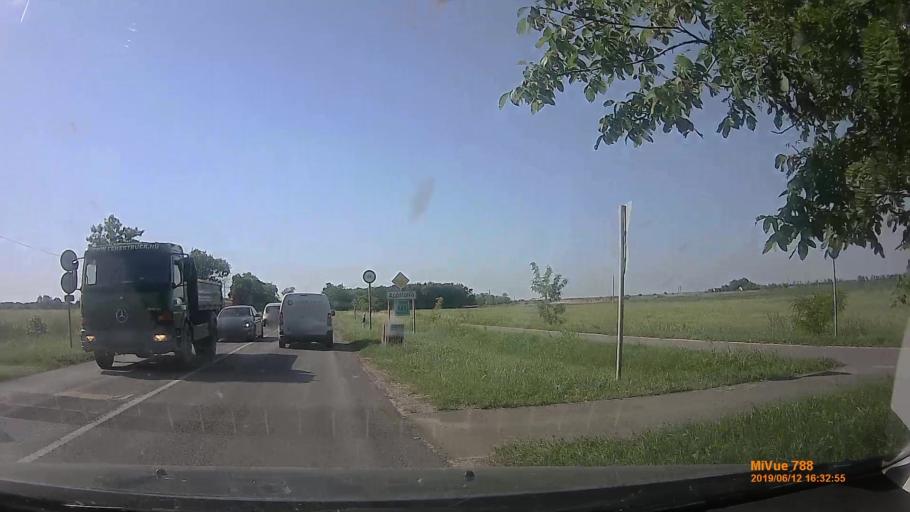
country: HU
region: Csongrad
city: Apatfalva
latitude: 46.1831
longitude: 20.5694
